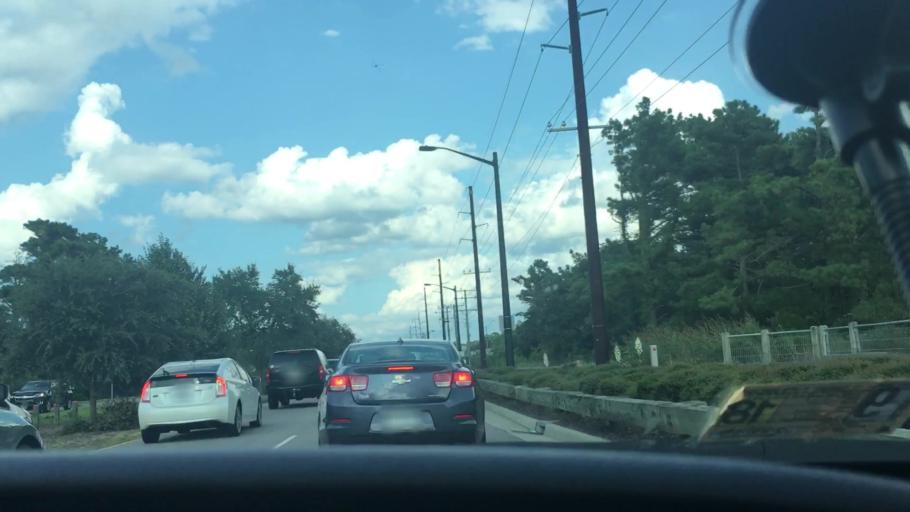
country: US
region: Virginia
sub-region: City of Virginia Beach
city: Virginia Beach
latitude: 36.9072
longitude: -76.1095
